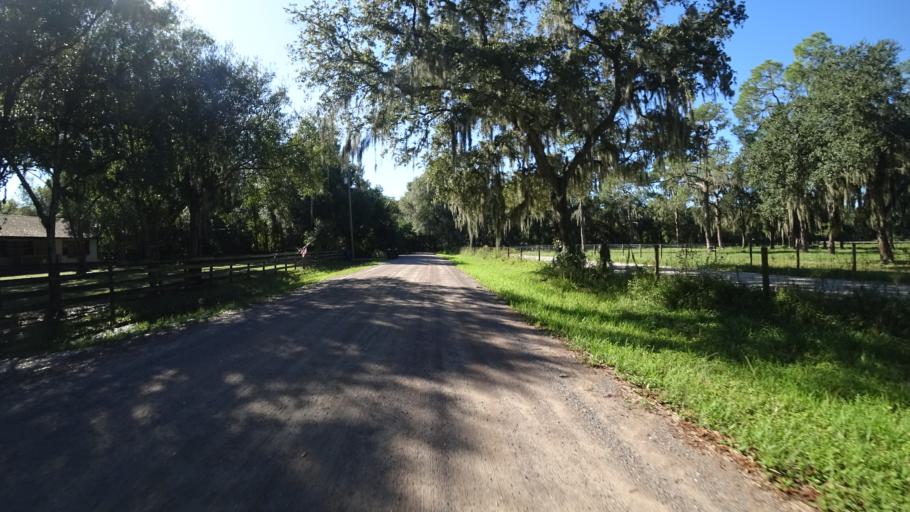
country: US
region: Florida
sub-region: Manatee County
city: Ellenton
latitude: 27.5757
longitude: -82.4418
